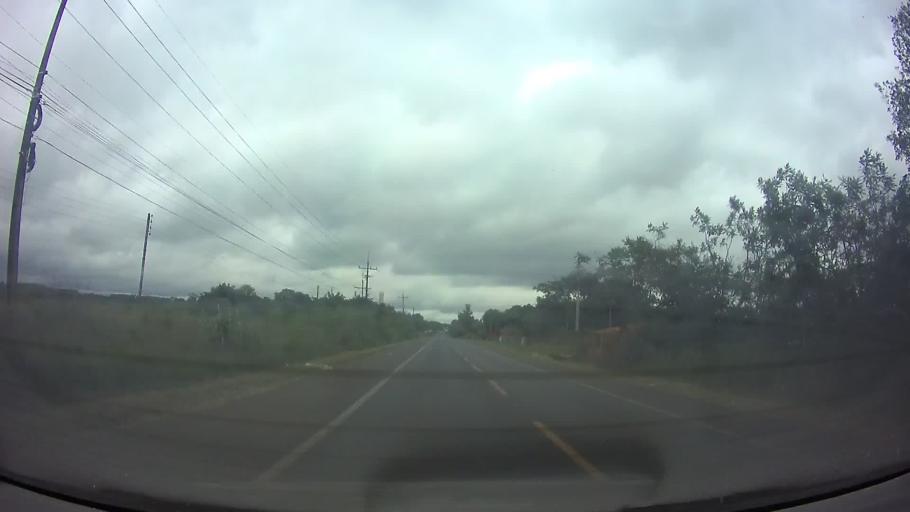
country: PY
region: Central
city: Guarambare
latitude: -25.4986
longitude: -57.4818
